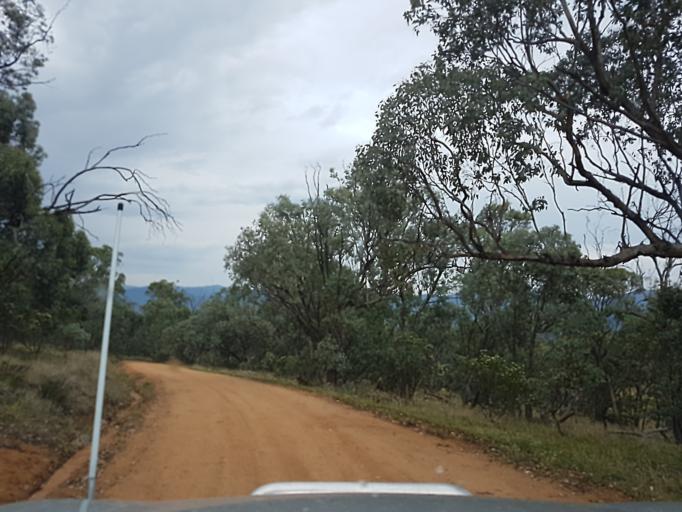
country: AU
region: New South Wales
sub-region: Snowy River
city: Jindabyne
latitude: -36.9563
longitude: 148.3610
